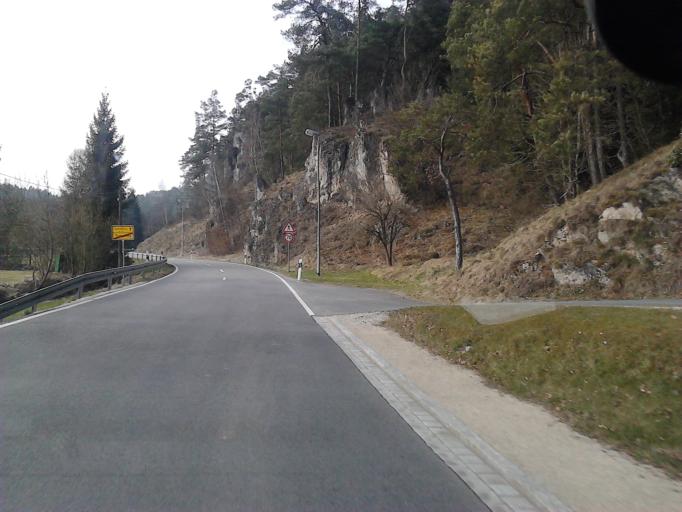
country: DE
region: Bavaria
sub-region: Upper Franconia
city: Stadelhofen
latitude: 49.9674
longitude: 11.1971
